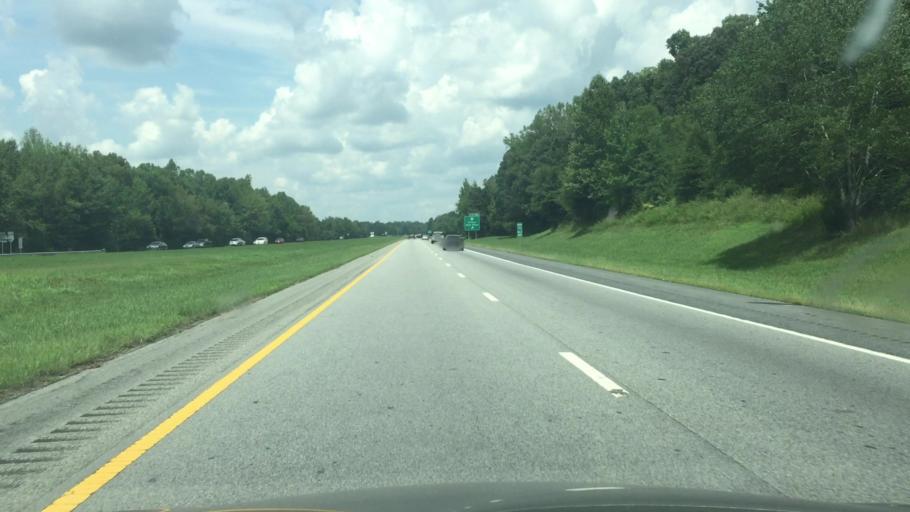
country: US
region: North Carolina
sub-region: Guilford County
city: Pleasant Garden
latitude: 35.9148
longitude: -79.8230
